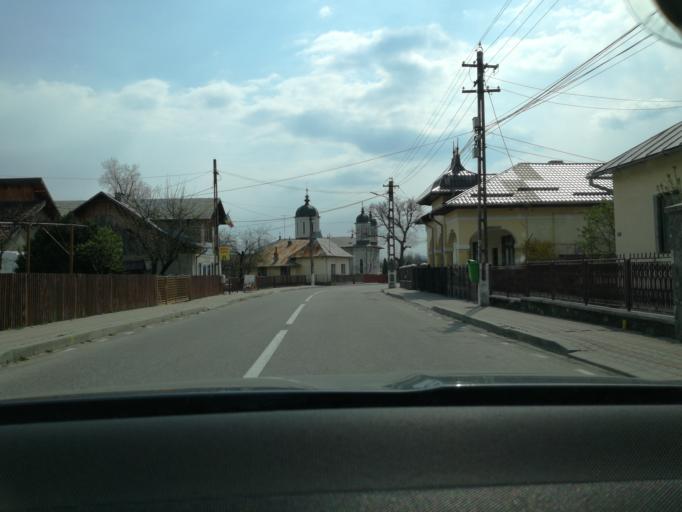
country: RO
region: Prahova
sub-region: Comuna Cornu
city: Cornu de Jos
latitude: 45.1538
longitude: 25.7042
